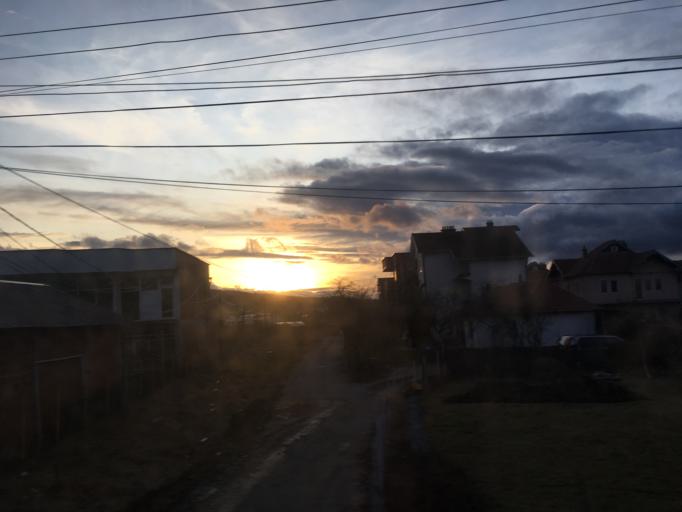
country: XK
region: Pristina
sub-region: Komuna e Drenasit
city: Glogovac
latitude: 42.5828
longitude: 20.8996
